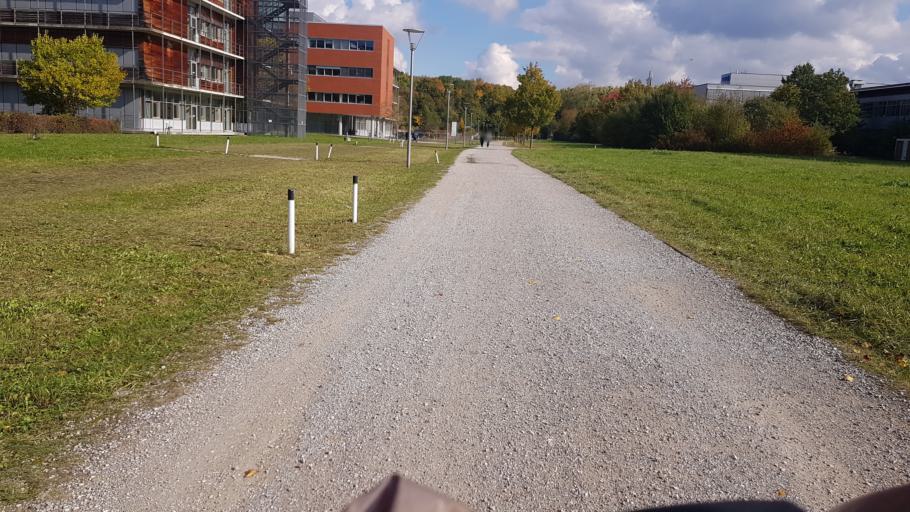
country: DE
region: Bavaria
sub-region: Upper Bavaria
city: Neuried
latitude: 48.1085
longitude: 11.4580
